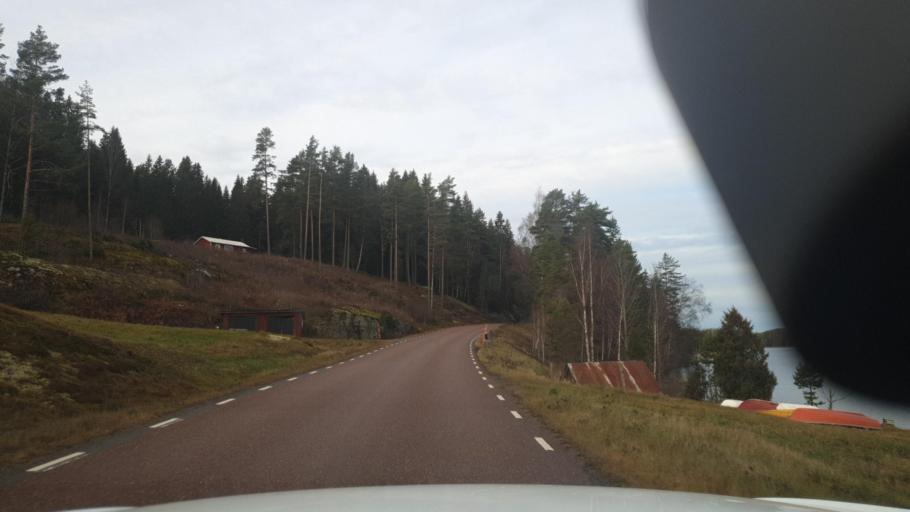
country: NO
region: Hedmark
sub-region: Eidskog
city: Skotterud
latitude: 59.7906
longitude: 12.0292
